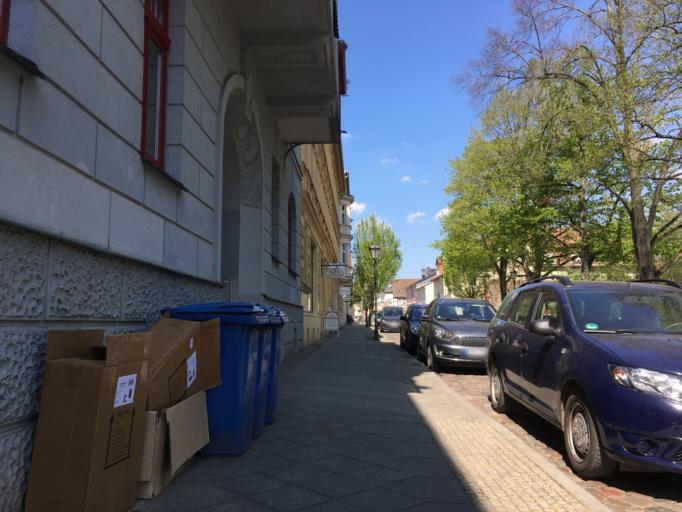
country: DE
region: Brandenburg
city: Bernau bei Berlin
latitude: 52.6767
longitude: 13.5904
